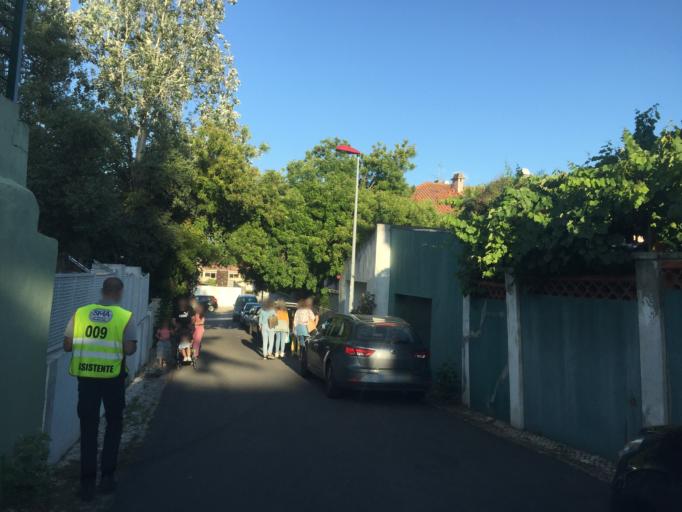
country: PT
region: Lisbon
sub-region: Odivelas
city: Pontinha
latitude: 38.7474
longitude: -9.2037
